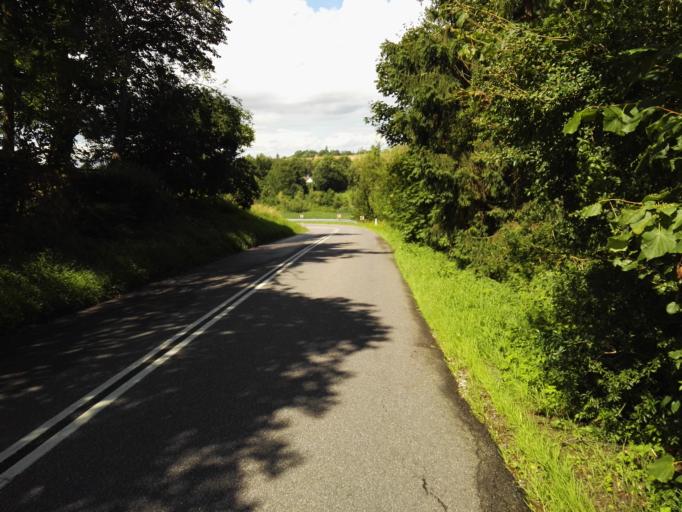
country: DK
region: Capital Region
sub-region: Egedal Kommune
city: Vekso
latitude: 55.7614
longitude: 12.2302
